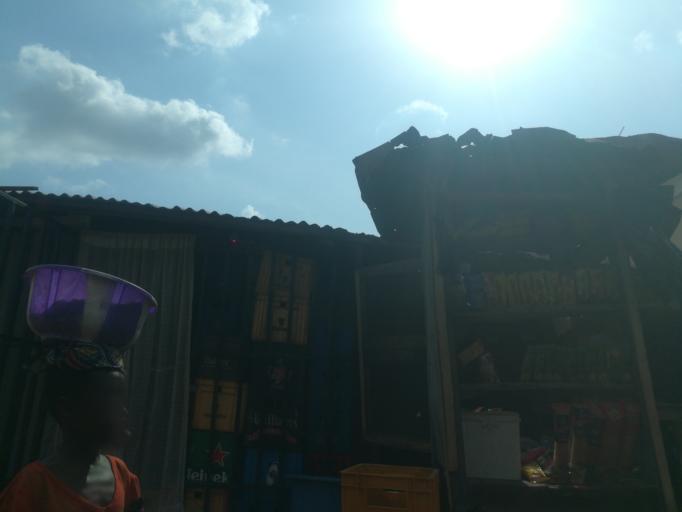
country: NG
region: Oyo
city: Ibadan
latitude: 7.3862
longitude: 3.8255
